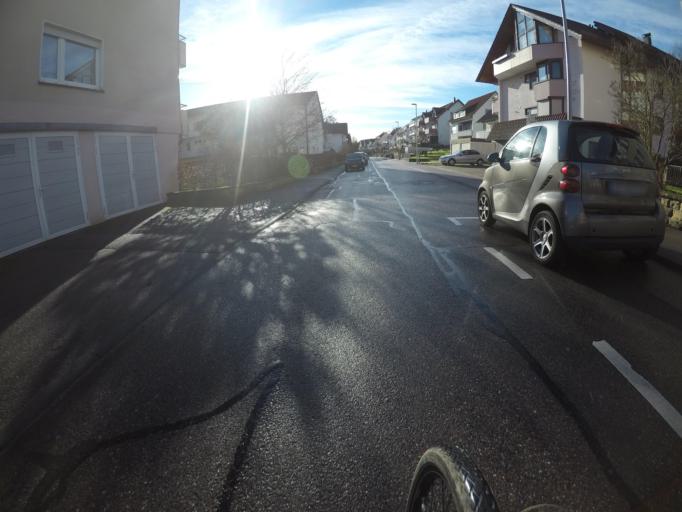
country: DE
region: Baden-Wuerttemberg
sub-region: Regierungsbezirk Stuttgart
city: Reichenbach an der Fils
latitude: 48.7106
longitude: 9.4554
